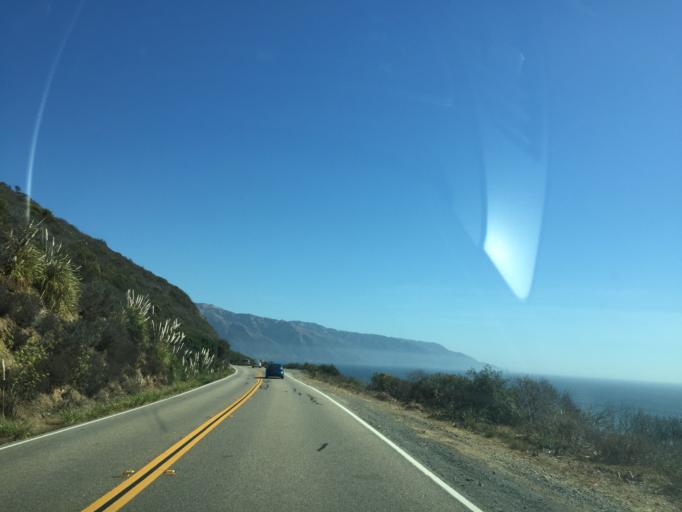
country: US
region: California
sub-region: Monterey County
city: Greenfield
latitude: 36.0236
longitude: -121.5701
